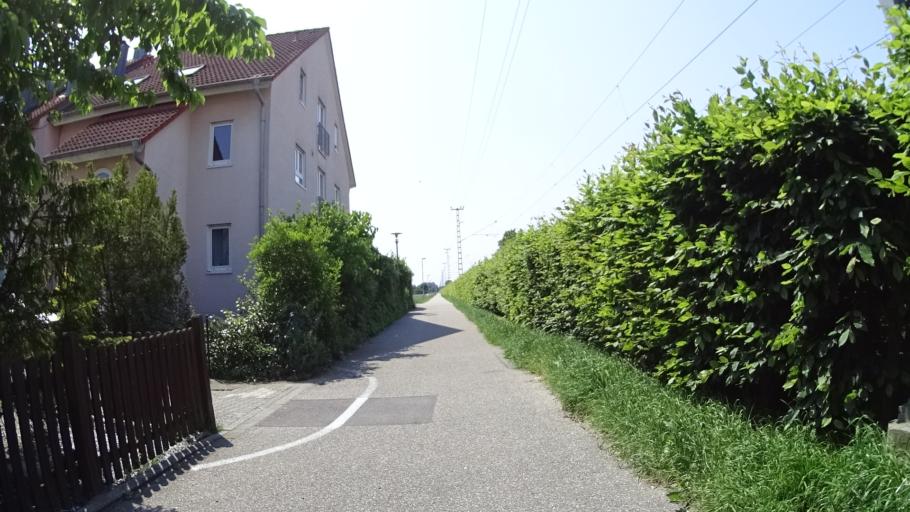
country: DE
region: Baden-Wuerttemberg
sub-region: Karlsruhe Region
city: Eggenstein-Leopoldshafen
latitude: 49.0825
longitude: 8.4009
